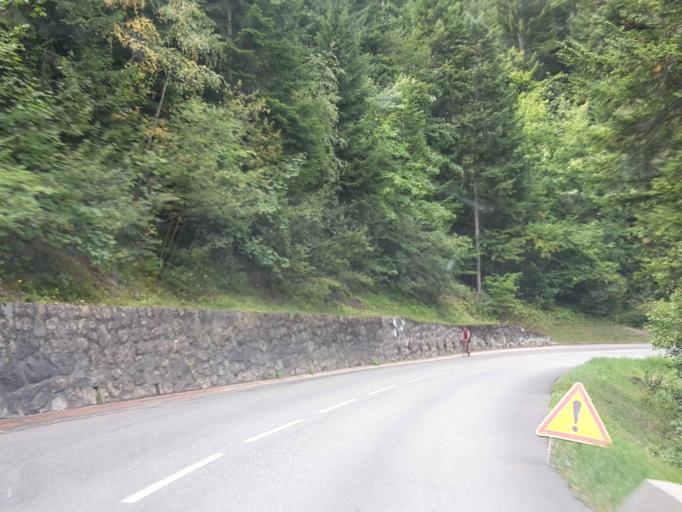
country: FR
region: Rhone-Alpes
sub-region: Departement de la Savoie
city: Saint-Michel-de-Maurienne
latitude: 45.2020
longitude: 6.4559
